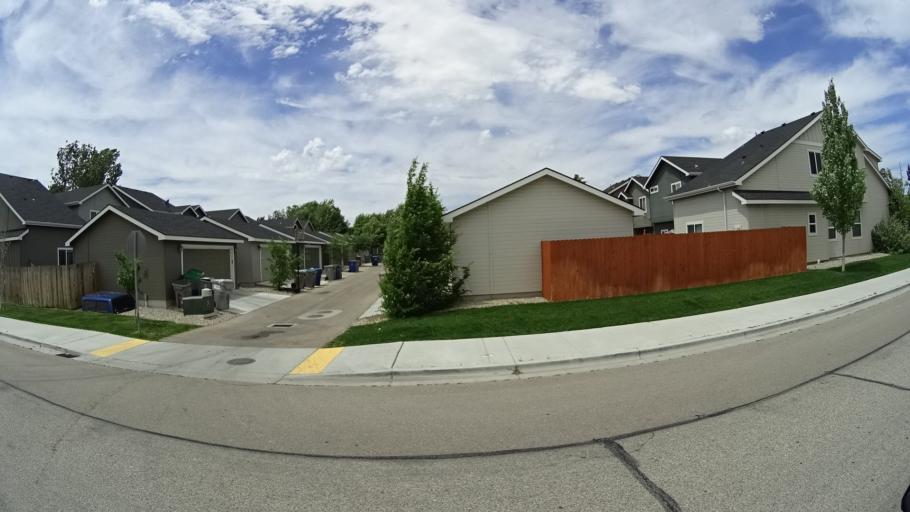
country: US
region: Idaho
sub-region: Ada County
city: Eagle
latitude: 43.6324
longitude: -116.3218
